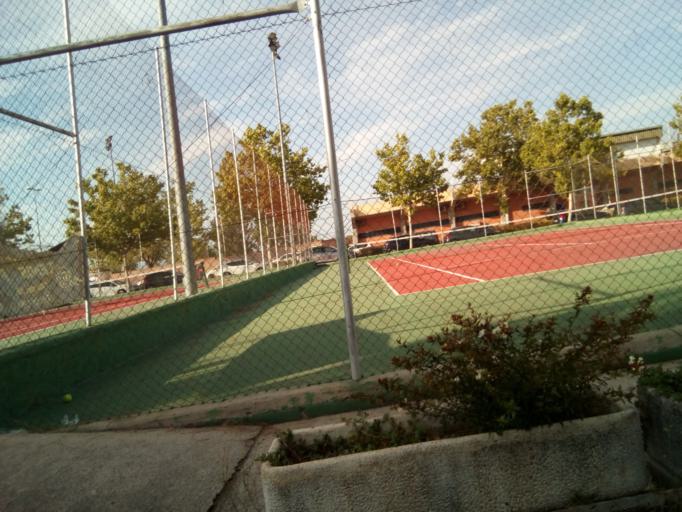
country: ES
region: Madrid
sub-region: Provincia de Madrid
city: Villanueva del Pardillo
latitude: 40.4829
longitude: -3.9745
